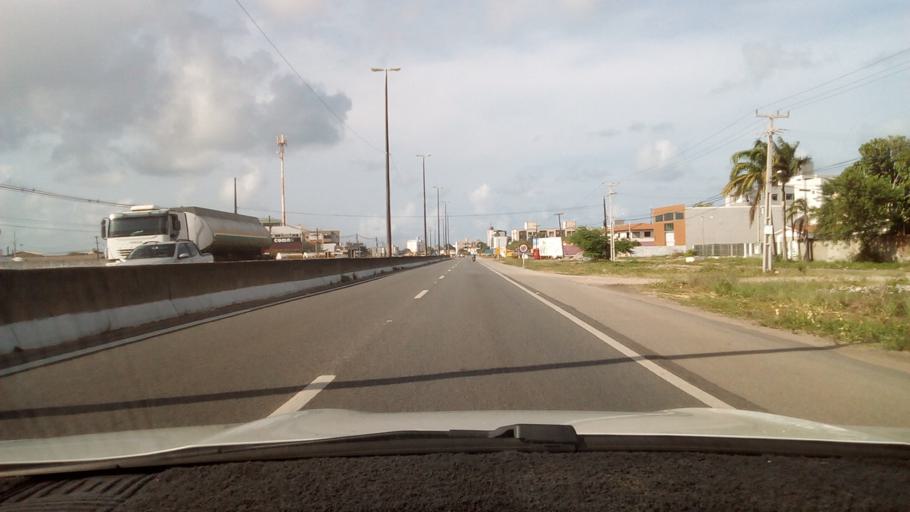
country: BR
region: Paraiba
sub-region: Cabedelo
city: Cabedelo
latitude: -7.0099
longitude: -34.8311
